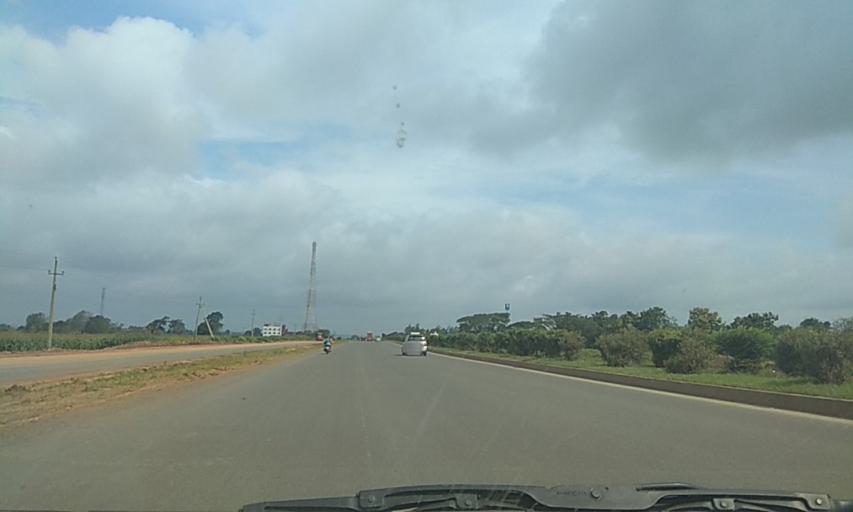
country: IN
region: Karnataka
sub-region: Dharwad
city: Kundgol
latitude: 15.1817
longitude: 75.1379
